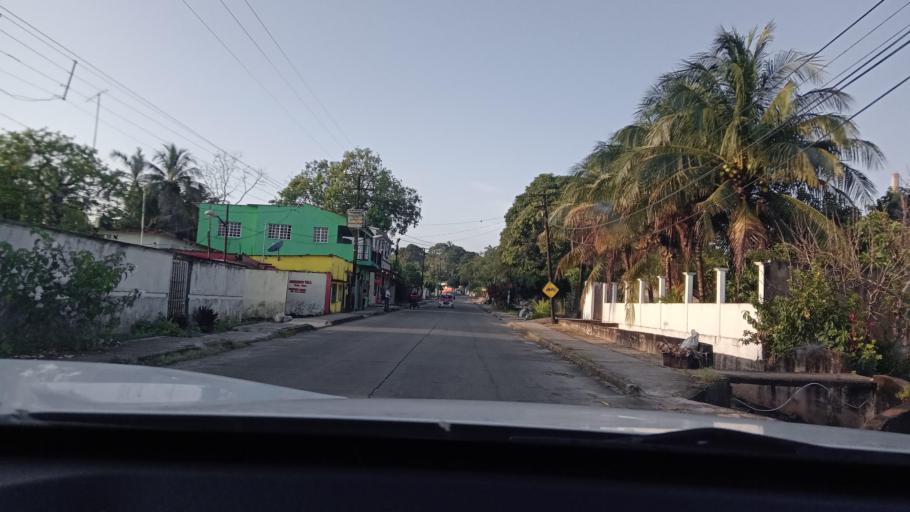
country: MX
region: Veracruz
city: Las Choapas
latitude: 17.8825
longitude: -94.0974
